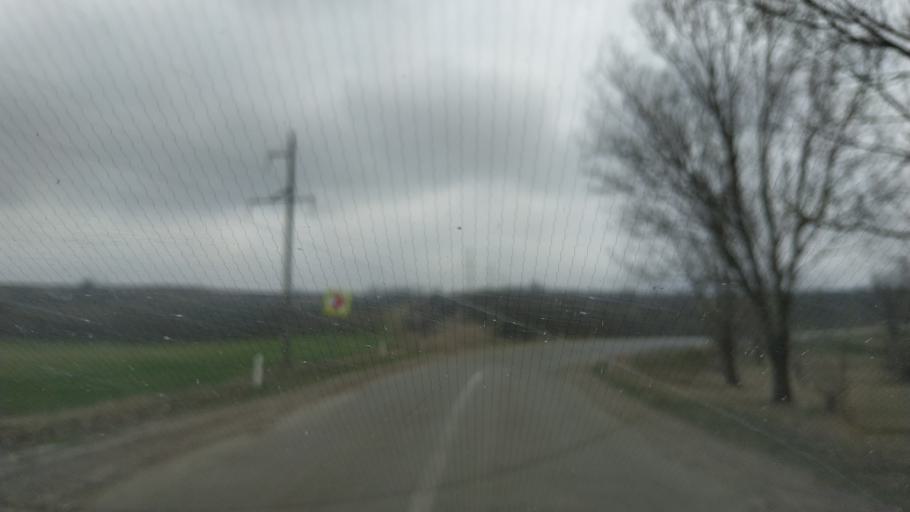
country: MD
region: Gagauzia
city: Bugeac
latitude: 46.3347
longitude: 28.7565
